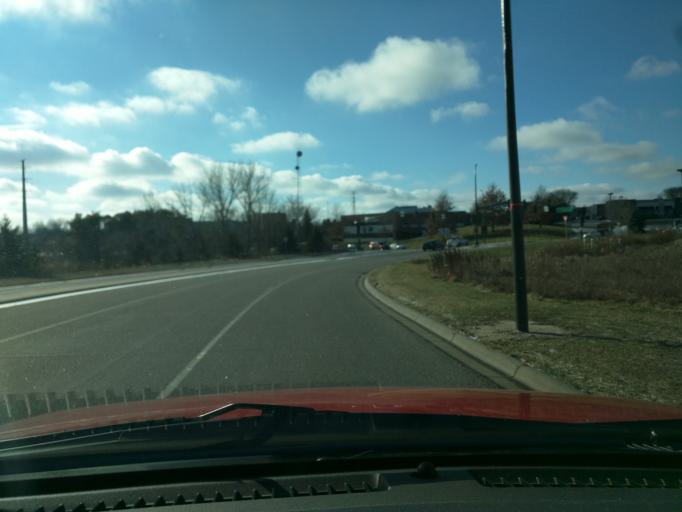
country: US
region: Minnesota
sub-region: Hennepin County
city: Eden Prairie
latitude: 44.8651
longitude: -93.4176
